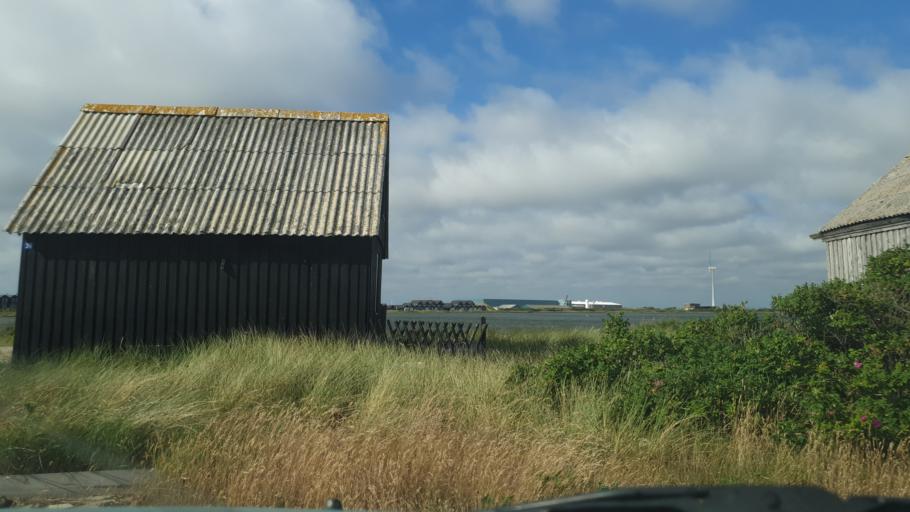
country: DK
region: Central Jutland
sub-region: Ringkobing-Skjern Kommune
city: Hvide Sande
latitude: 56.0018
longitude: 8.1328
